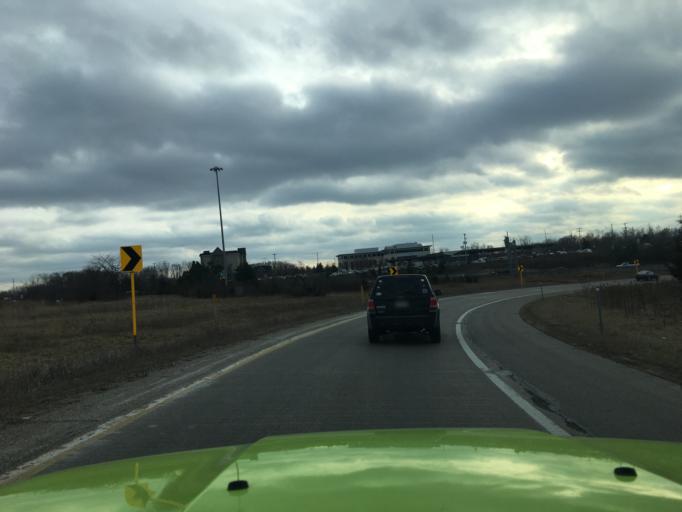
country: US
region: Michigan
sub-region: Kent County
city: East Grand Rapids
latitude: 42.9737
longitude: -85.5887
